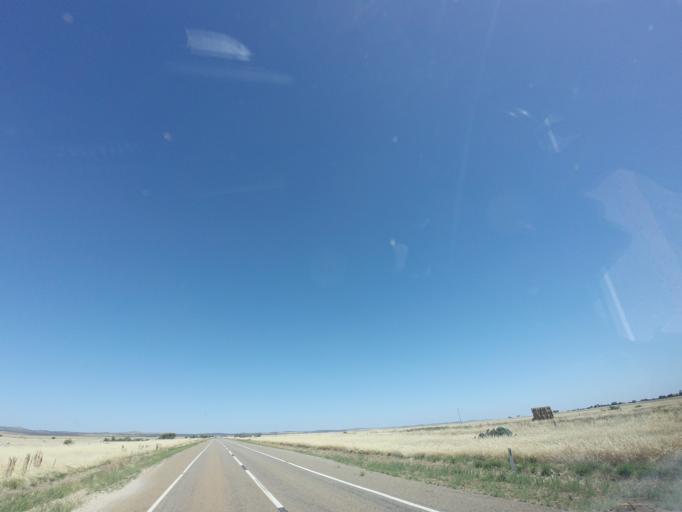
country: AU
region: South Australia
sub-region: Peterborough
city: Peterborough
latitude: -32.8203
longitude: 138.6963
